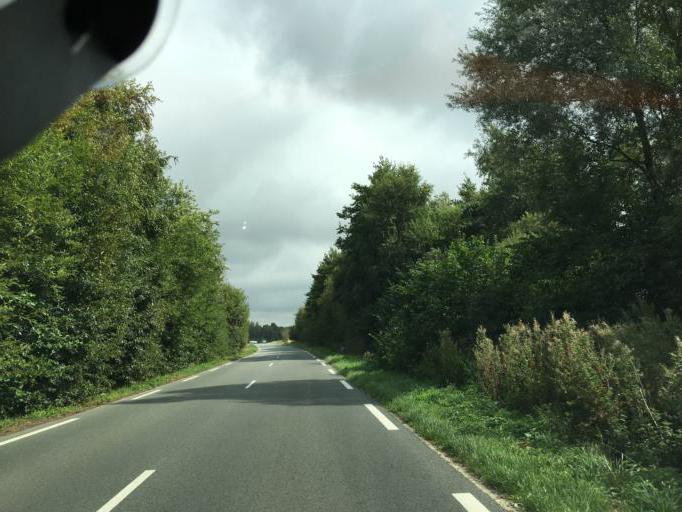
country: FR
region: Nord-Pas-de-Calais
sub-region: Departement du Pas-de-Calais
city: Saint-Josse
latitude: 50.4307
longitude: 1.7021
